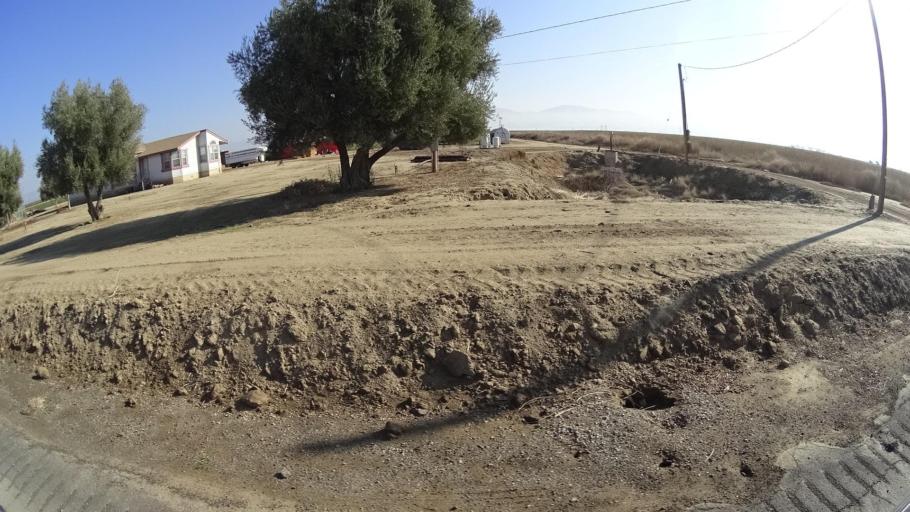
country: US
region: California
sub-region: Kern County
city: Weedpatch
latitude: 35.2160
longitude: -118.9322
